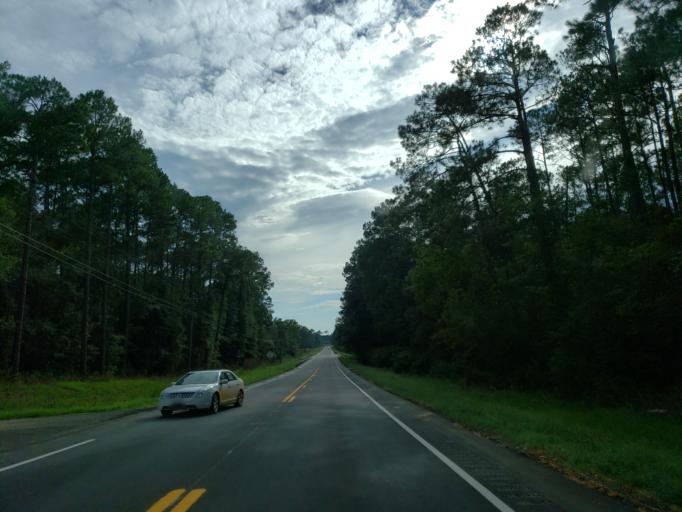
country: US
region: Georgia
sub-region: Irwin County
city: Ocilla
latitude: 31.5653
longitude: -83.3168
